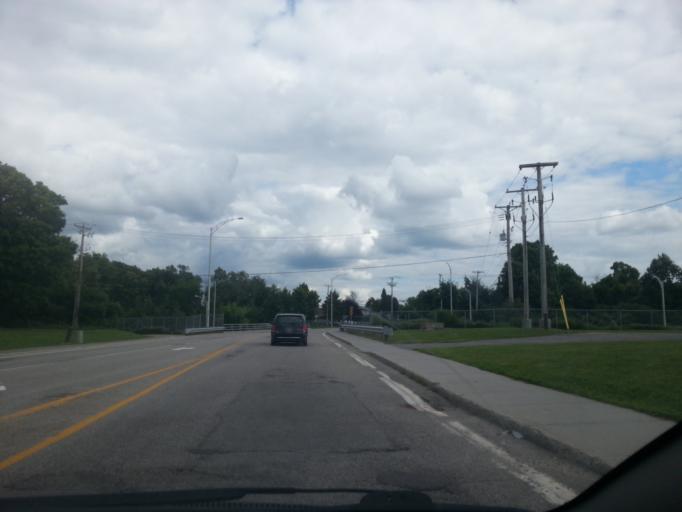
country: CA
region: Quebec
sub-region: Outaouais
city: Gatineau
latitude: 45.4923
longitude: -75.7390
